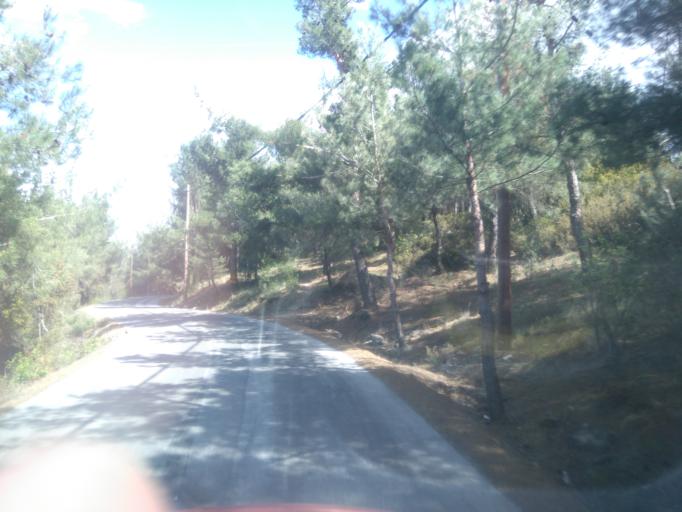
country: GR
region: Central Macedonia
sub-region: Nomos Thessalonikis
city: Asvestochori
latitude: 40.6407
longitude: 23.0084
